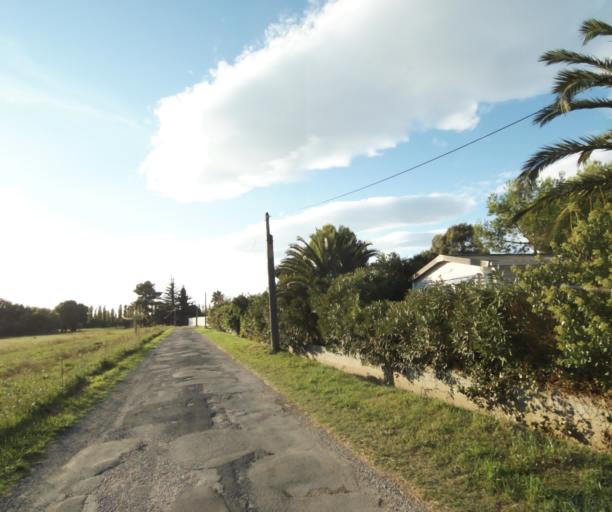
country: FR
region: Languedoc-Roussillon
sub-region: Departement des Pyrenees-Orientales
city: Argelers
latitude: 42.5715
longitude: 3.0382
